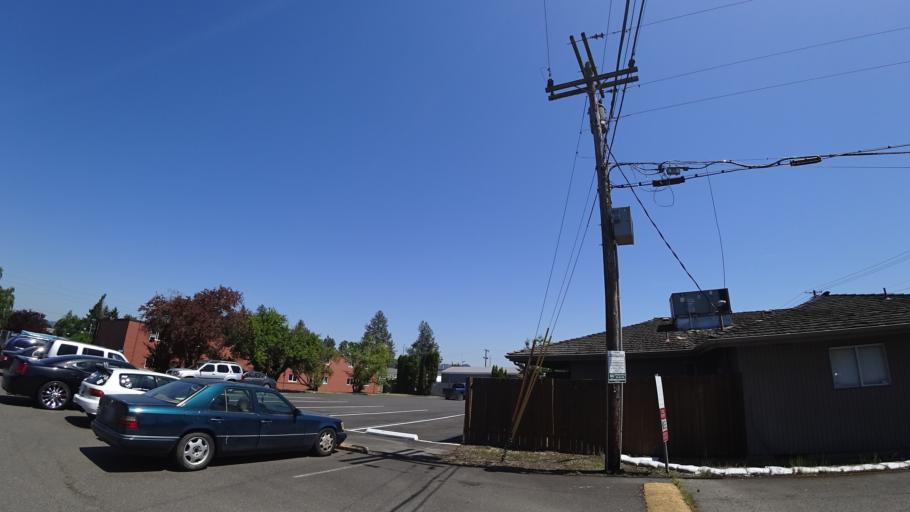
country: US
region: Oregon
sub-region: Washington County
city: Beaverton
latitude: 45.4873
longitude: -122.8190
